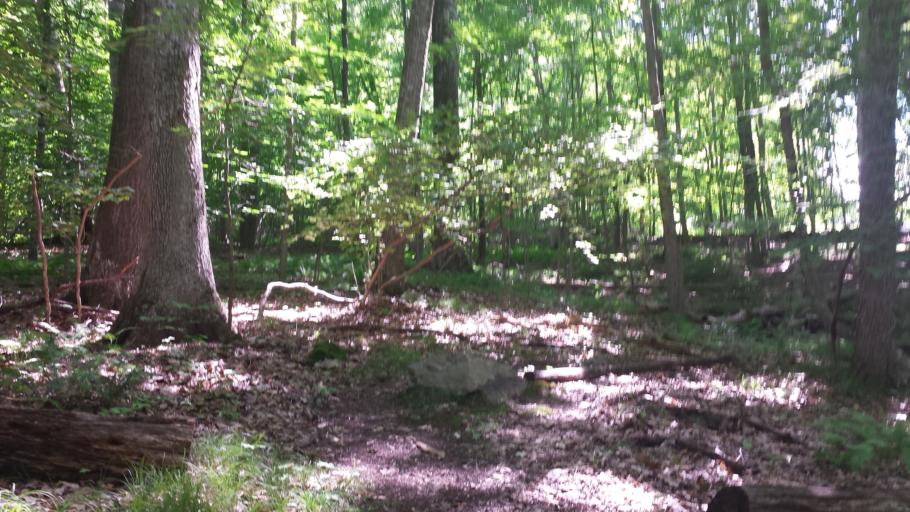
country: US
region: New York
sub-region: Westchester County
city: Pound Ridge
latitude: 41.2585
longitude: -73.5832
